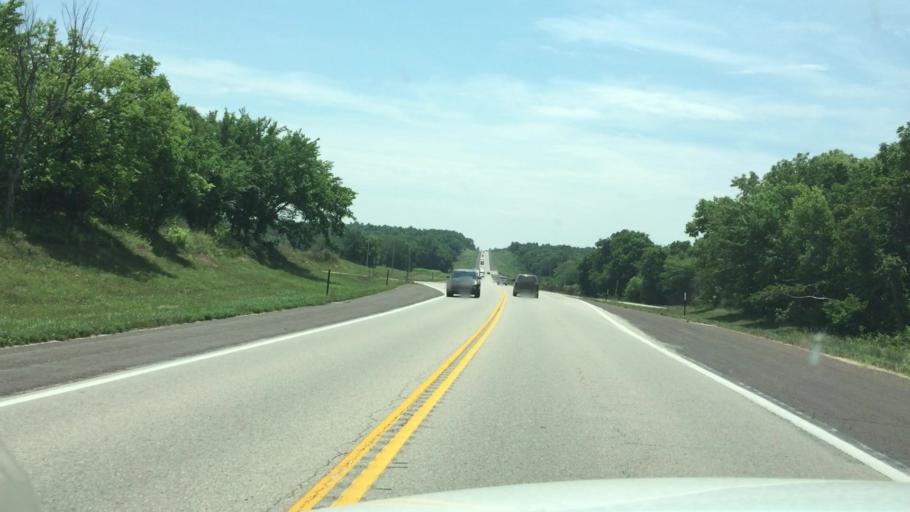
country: US
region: Kansas
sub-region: Jackson County
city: Holton
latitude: 39.5514
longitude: -95.7483
